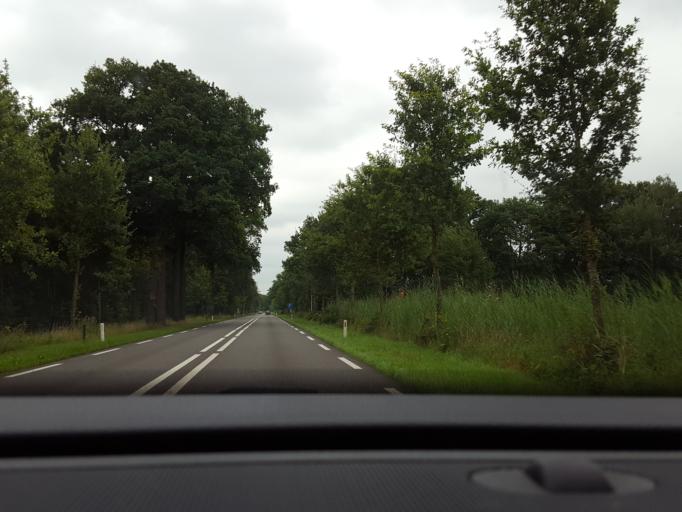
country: NL
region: Gelderland
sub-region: Gemeente Rheden
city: Spankeren
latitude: 52.0887
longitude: 6.1198
